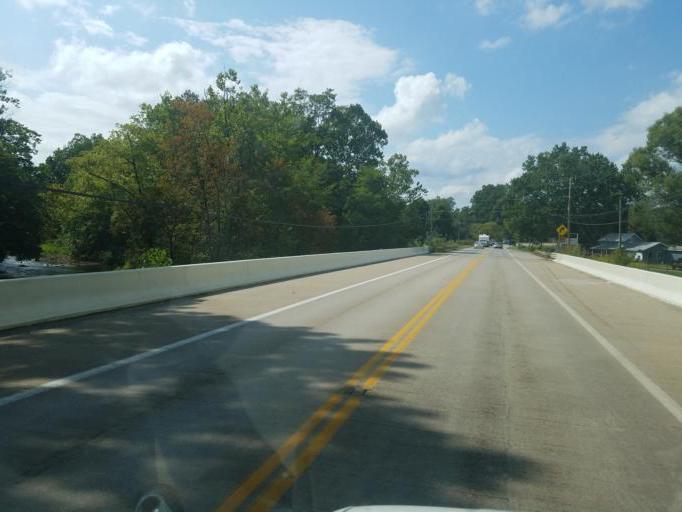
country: US
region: Ohio
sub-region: Sandusky County
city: Bellville
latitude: 40.5981
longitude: -82.4427
